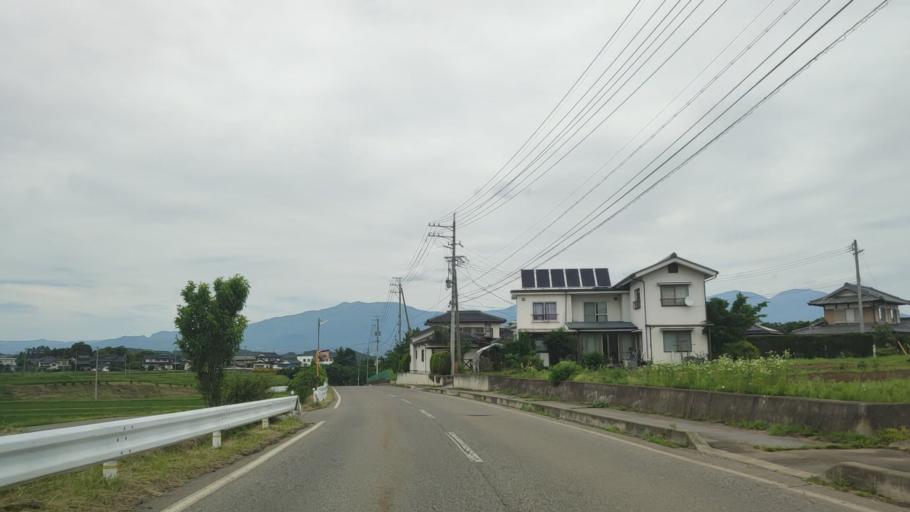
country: JP
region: Nagano
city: Kamimaruko
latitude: 36.2952
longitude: 138.3178
